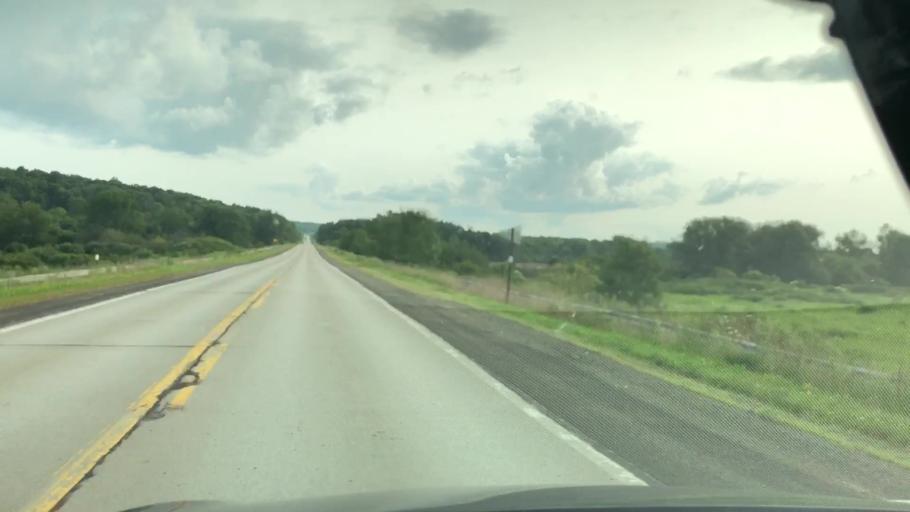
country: US
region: Pennsylvania
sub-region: Erie County
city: Union City
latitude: 41.9822
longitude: -79.8377
